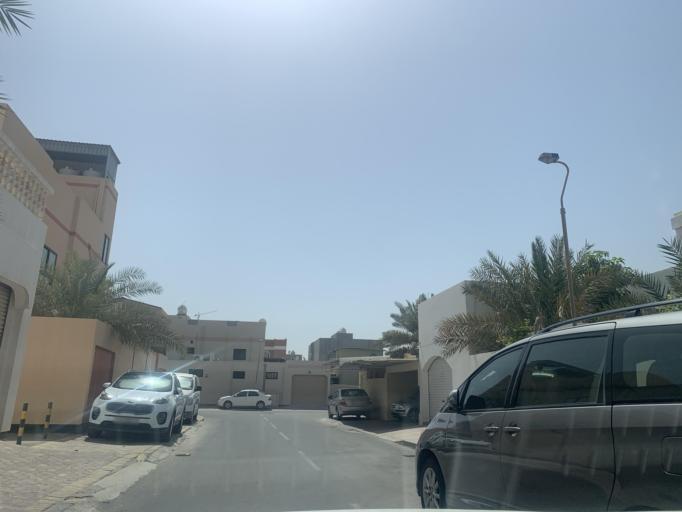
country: BH
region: Manama
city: Jidd Hafs
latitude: 26.2259
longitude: 50.5486
